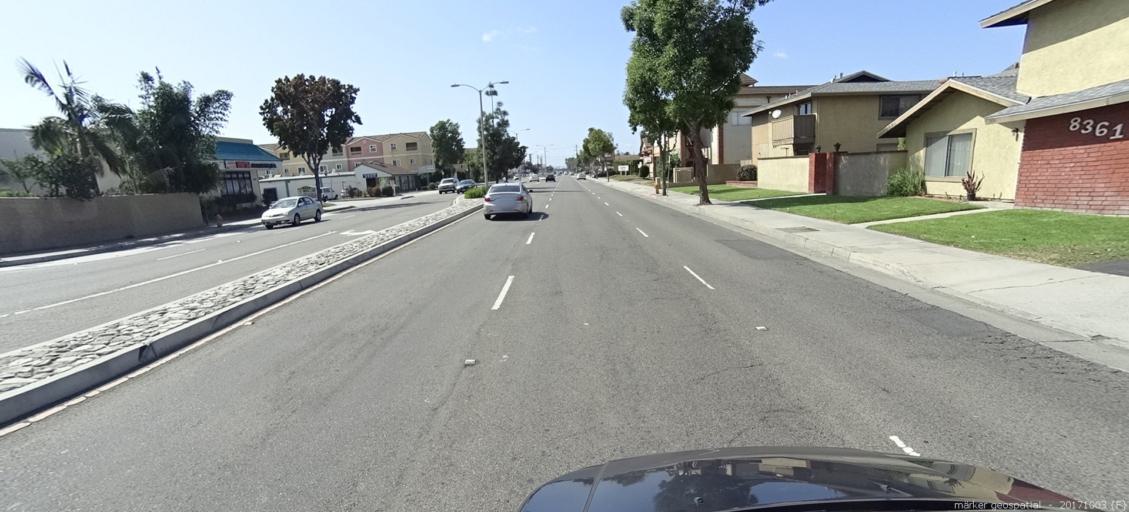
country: US
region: California
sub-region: Orange County
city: Westminster
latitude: 33.7739
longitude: -117.9857
